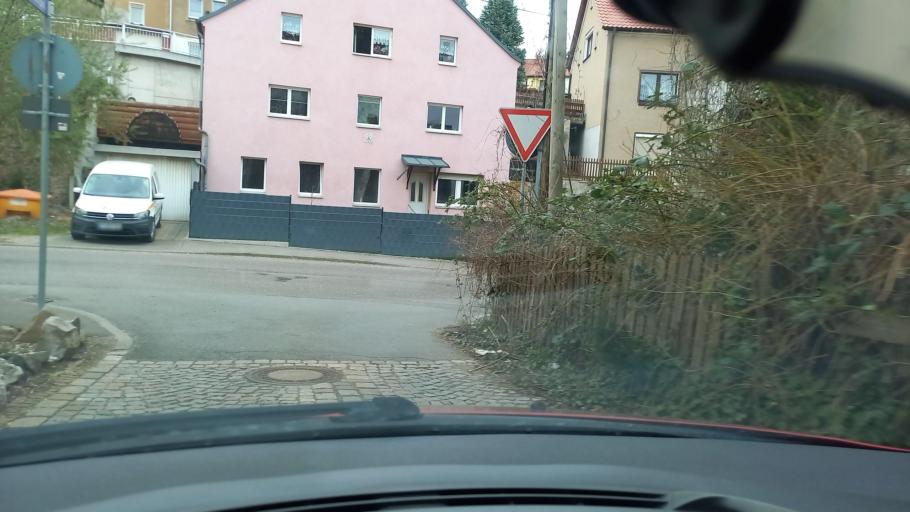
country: DE
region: Saxony
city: Wilkau-Hasslau
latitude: 50.6822
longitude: 12.4942
